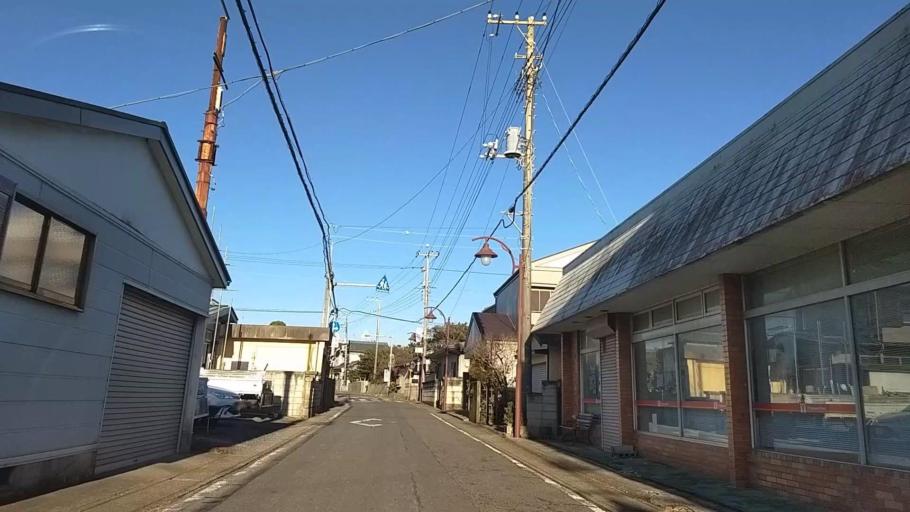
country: JP
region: Chiba
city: Asahi
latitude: 35.6989
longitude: 140.7257
